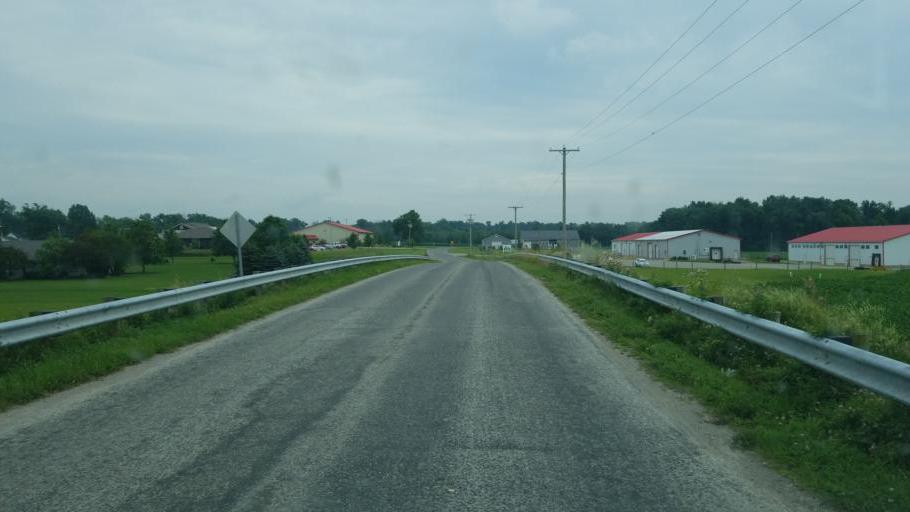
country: US
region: Ohio
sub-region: Wayne County
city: Orrville
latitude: 40.7960
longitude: -81.7776
